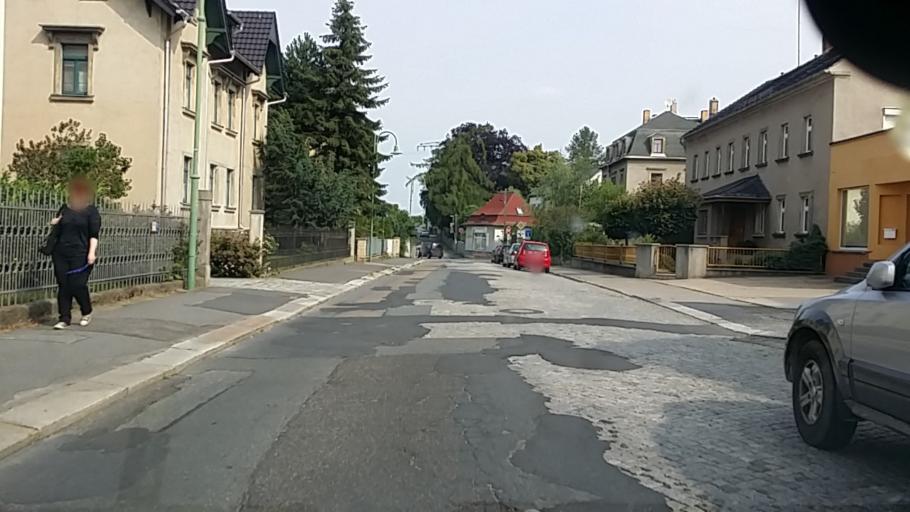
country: DE
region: Saxony
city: Radeberg
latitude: 51.1252
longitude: 13.9142
